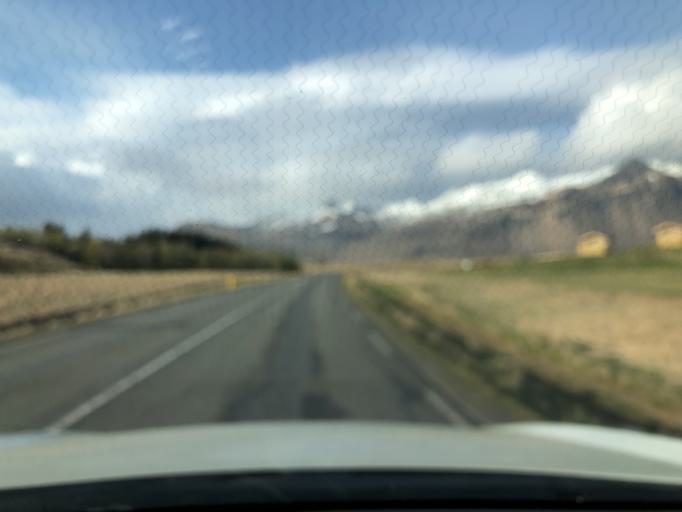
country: IS
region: East
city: Hoefn
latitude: 64.2835
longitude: -15.1885
